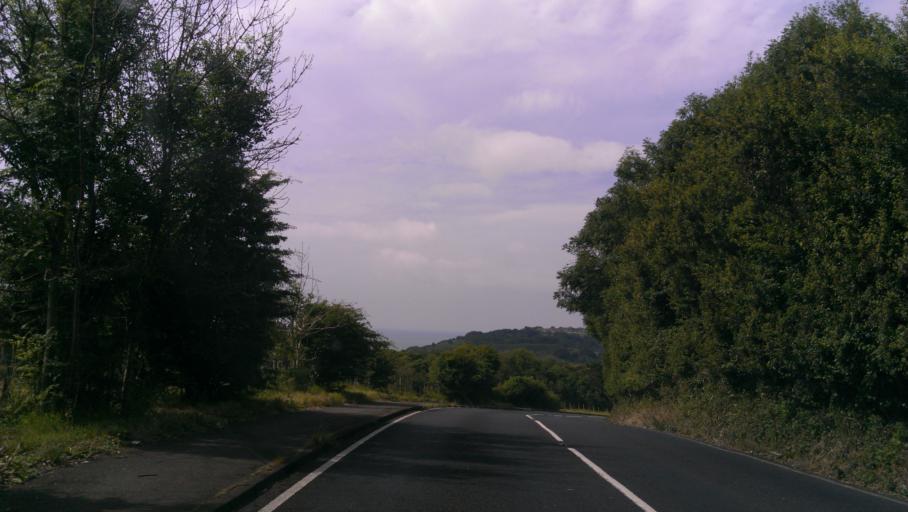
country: GB
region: England
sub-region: Kent
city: Dover
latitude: 51.1338
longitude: 1.3232
